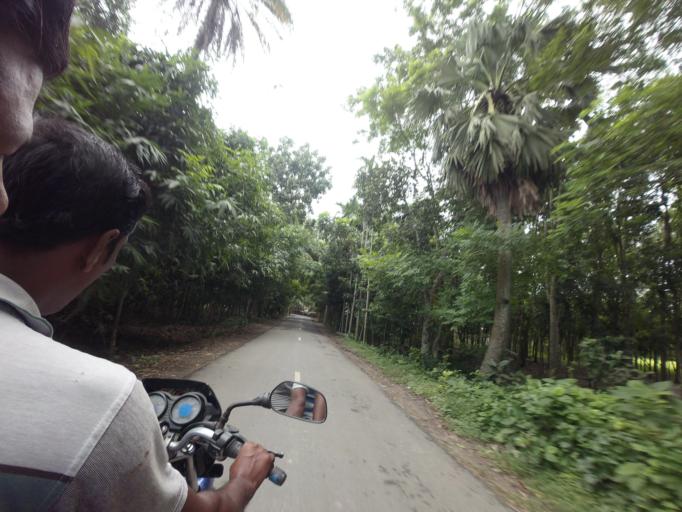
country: BD
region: Khulna
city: Kalia
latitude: 23.1173
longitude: 89.6477
